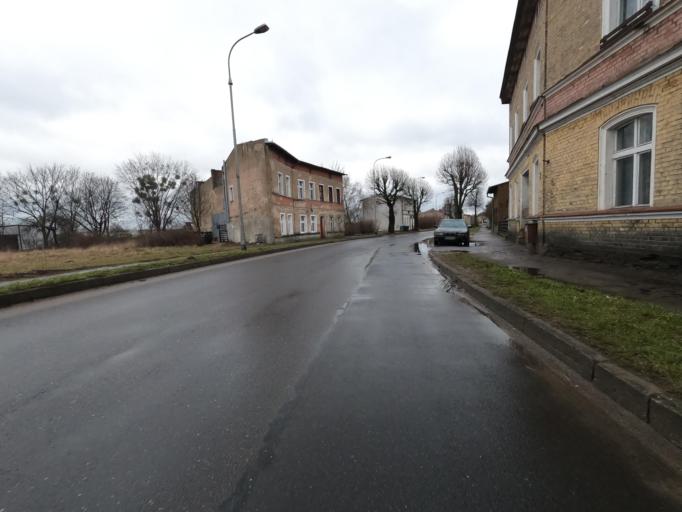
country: PL
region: Greater Poland Voivodeship
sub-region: Powiat pilski
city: Pila
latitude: 53.1430
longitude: 16.7577
